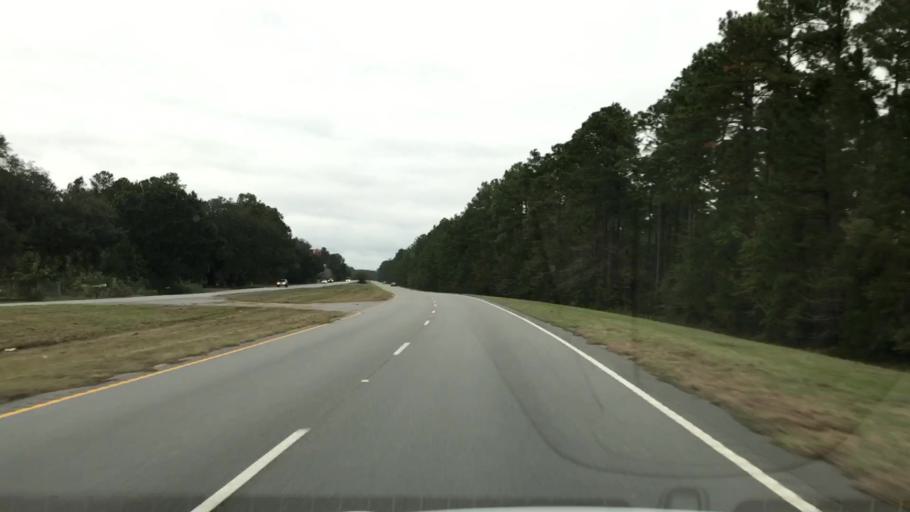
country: US
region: South Carolina
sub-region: Georgetown County
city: Georgetown
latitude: 33.2314
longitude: -79.3761
